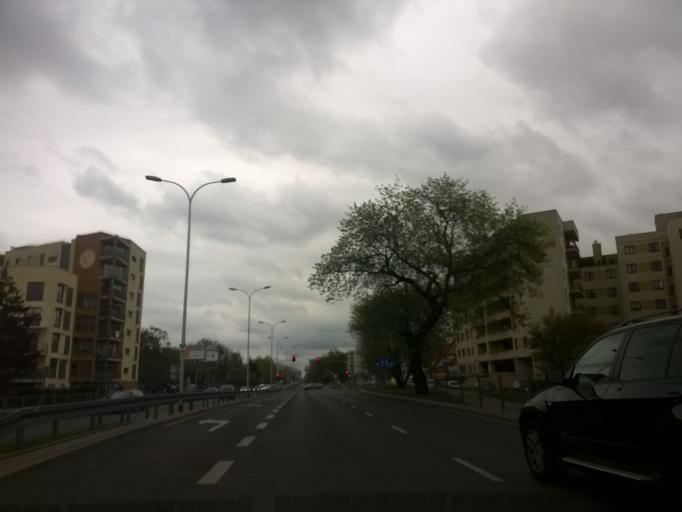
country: PL
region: Masovian Voivodeship
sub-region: Warszawa
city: Mokotow
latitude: 52.1743
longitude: 21.0476
